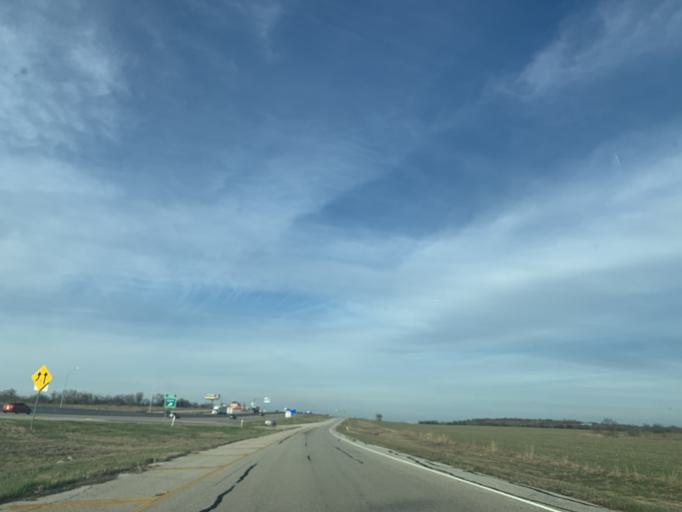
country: US
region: Texas
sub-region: Bell County
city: Salado
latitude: 30.8764
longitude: -97.5797
